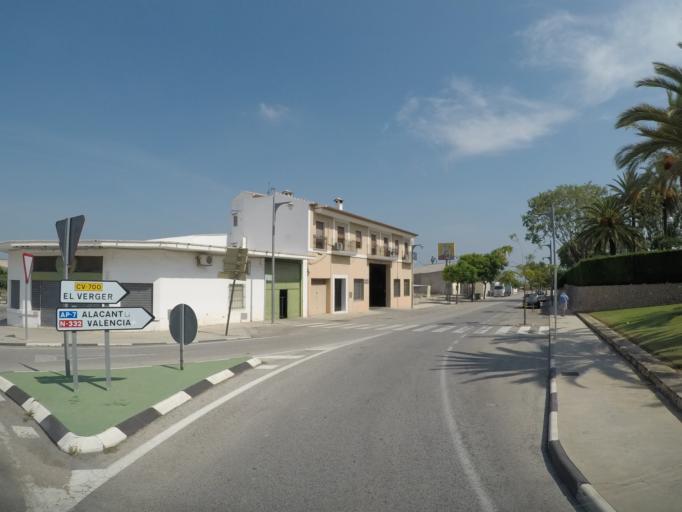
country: ES
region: Valencia
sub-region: Provincia de Alicante
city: Pego
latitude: 38.8435
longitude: -0.1100
